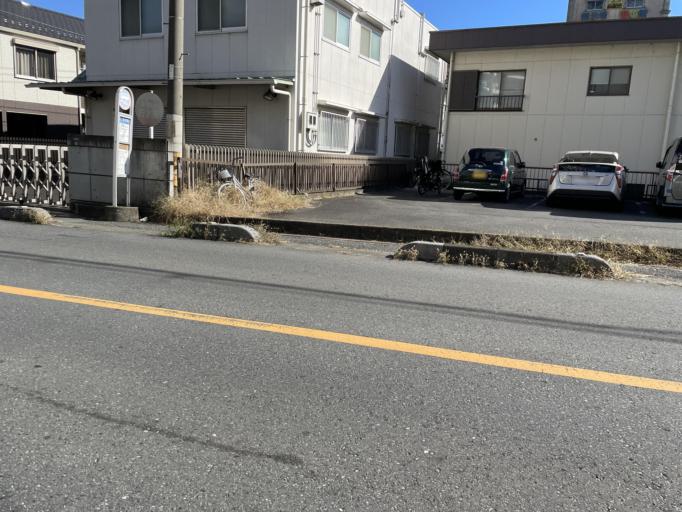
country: JP
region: Saitama
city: Wako
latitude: 35.7878
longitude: 139.6293
